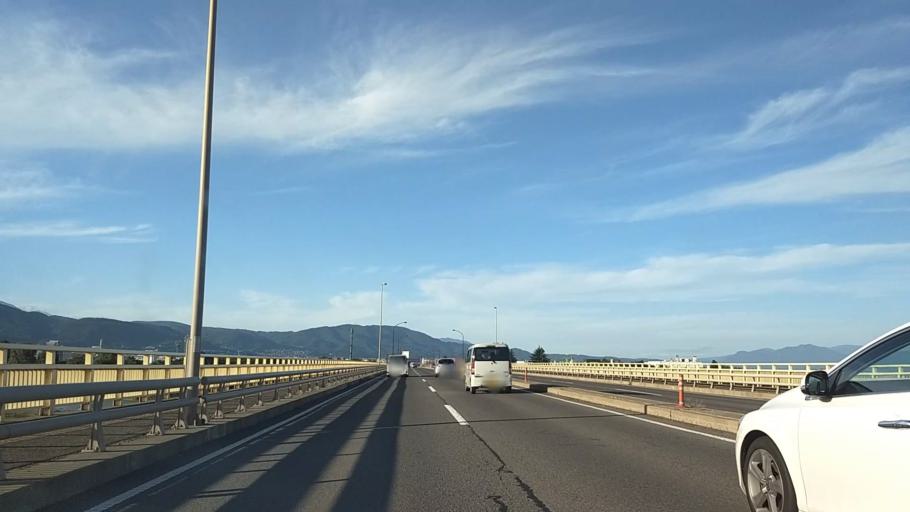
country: JP
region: Nagano
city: Nagano-shi
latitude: 36.6174
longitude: 138.1982
